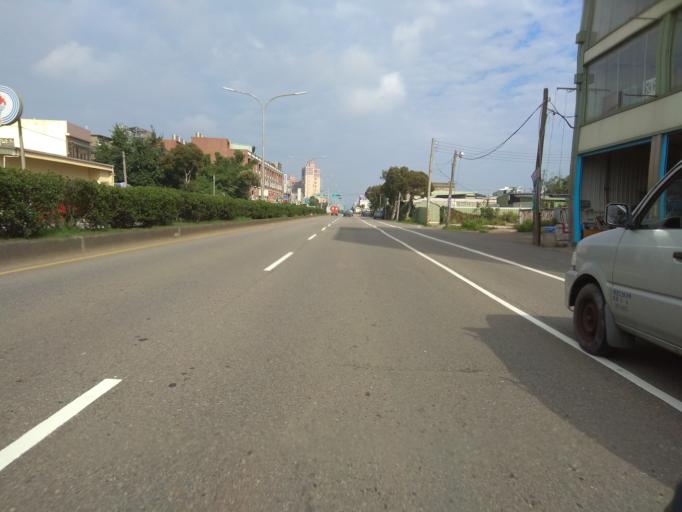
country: TW
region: Taiwan
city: Taoyuan City
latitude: 25.0526
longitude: 121.1532
